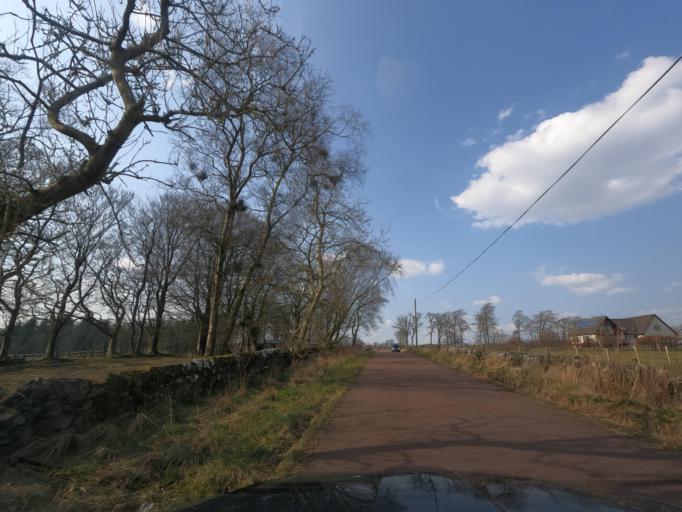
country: GB
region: Scotland
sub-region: South Lanarkshire
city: Carnwath
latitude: 55.7462
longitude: -3.6361
